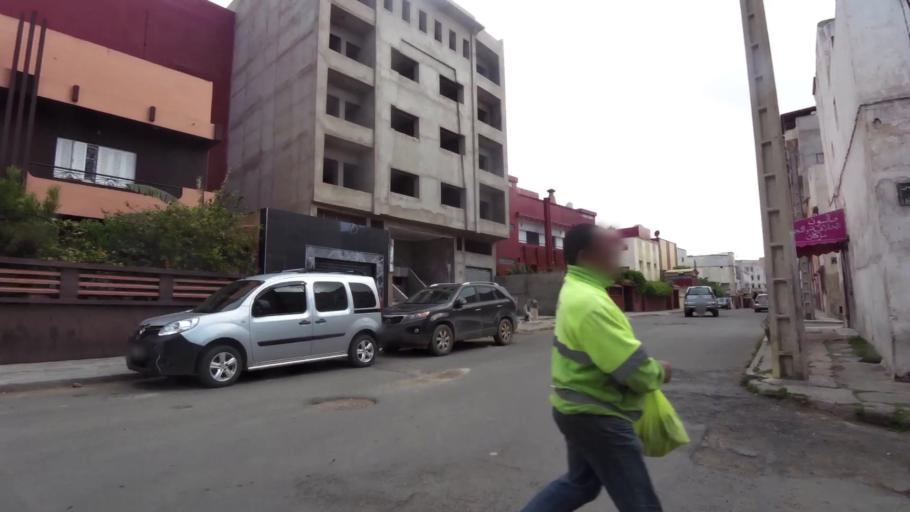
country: MA
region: Doukkala-Abda
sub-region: El-Jadida
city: El Jadida
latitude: 33.2454
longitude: -8.4970
